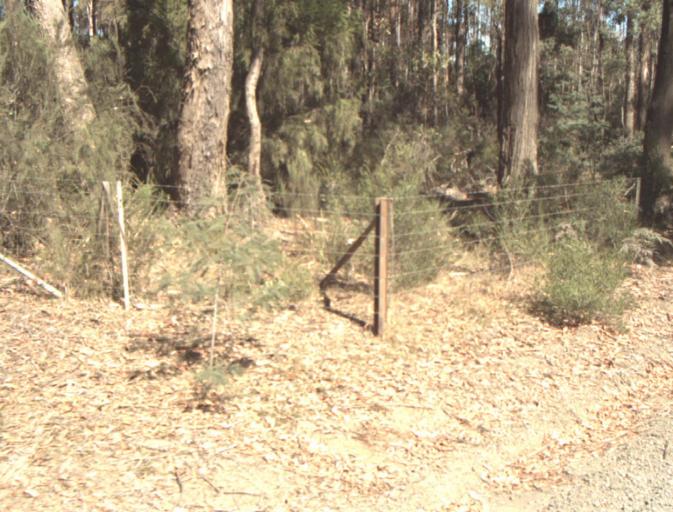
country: AU
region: Tasmania
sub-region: Launceston
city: Newstead
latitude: -41.3751
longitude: 147.2848
